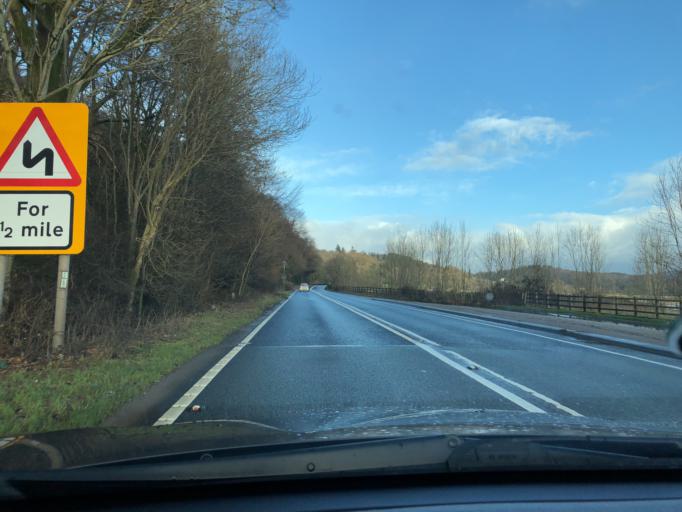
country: GB
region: England
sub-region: Cumbria
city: Ulverston
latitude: 54.2390
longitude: -3.0483
